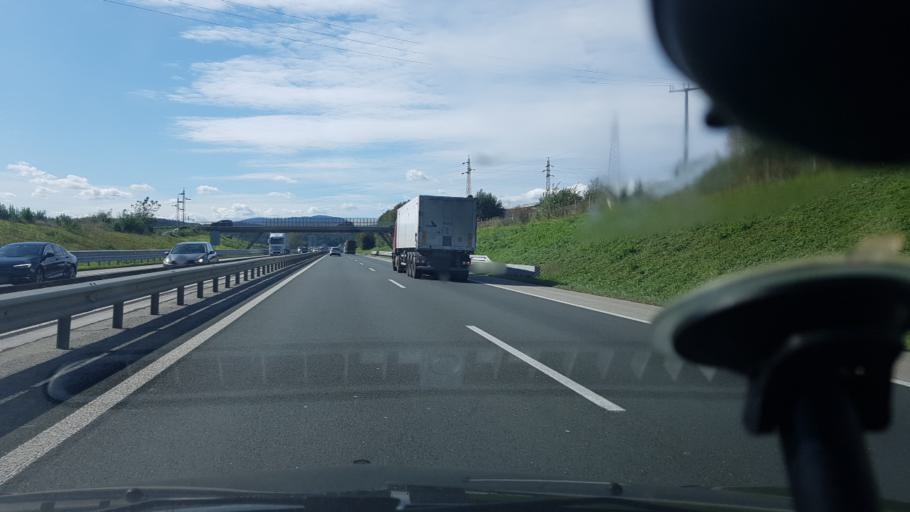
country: SI
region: Slovenska Bistrica
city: Slovenska Bistrica
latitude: 46.3808
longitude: 15.5674
